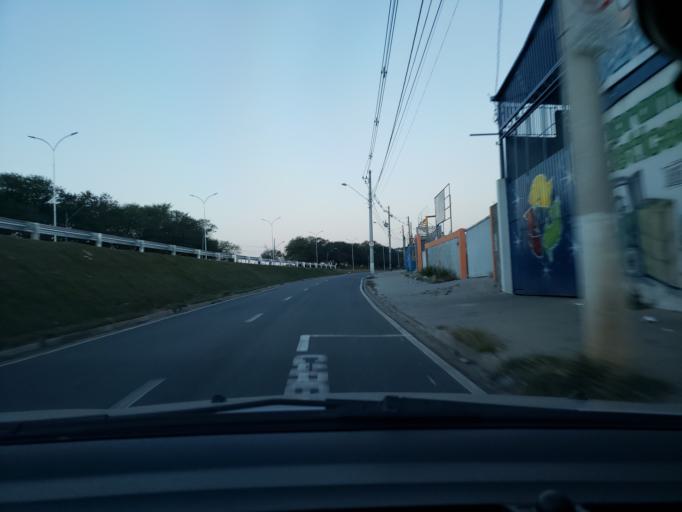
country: BR
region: Sao Paulo
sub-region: Campinas
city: Campinas
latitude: -22.9364
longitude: -47.1404
